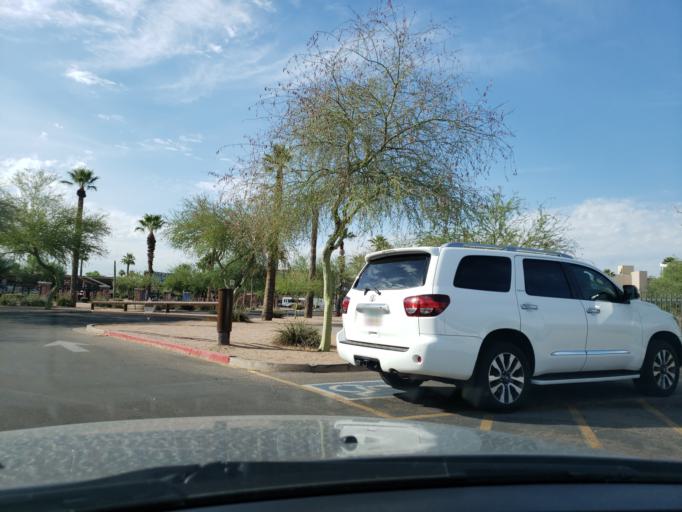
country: US
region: Arizona
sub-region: Maricopa County
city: Phoenix
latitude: 33.4962
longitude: -112.0697
